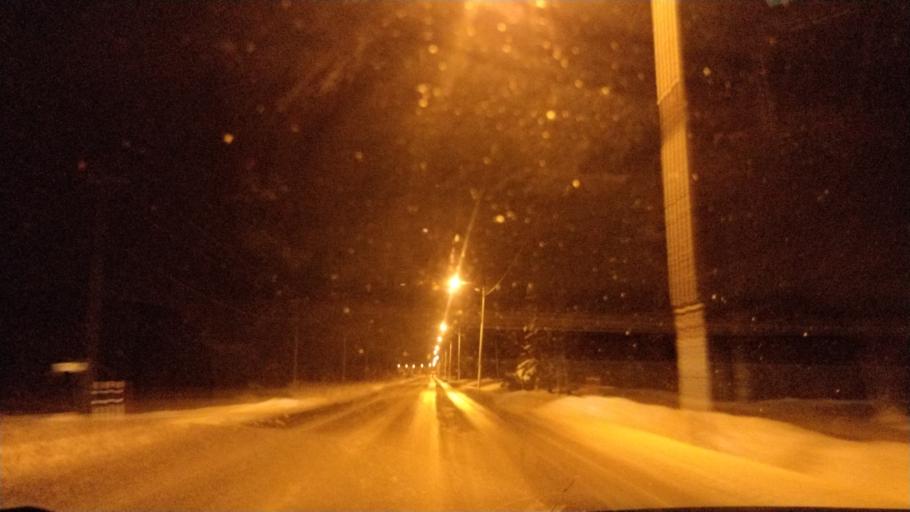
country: FI
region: Lapland
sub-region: Rovaniemi
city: Rovaniemi
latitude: 66.3076
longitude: 25.3595
